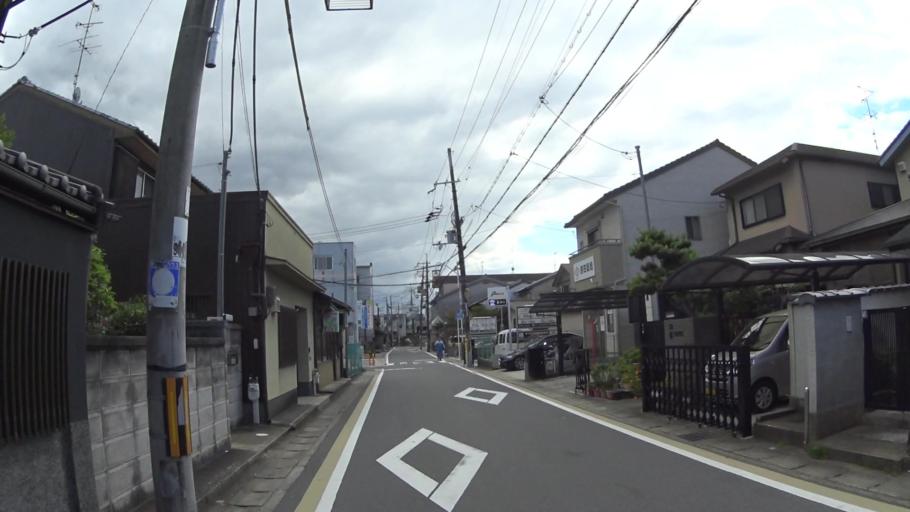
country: JP
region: Kyoto
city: Yawata
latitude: 34.9032
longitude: 135.7203
